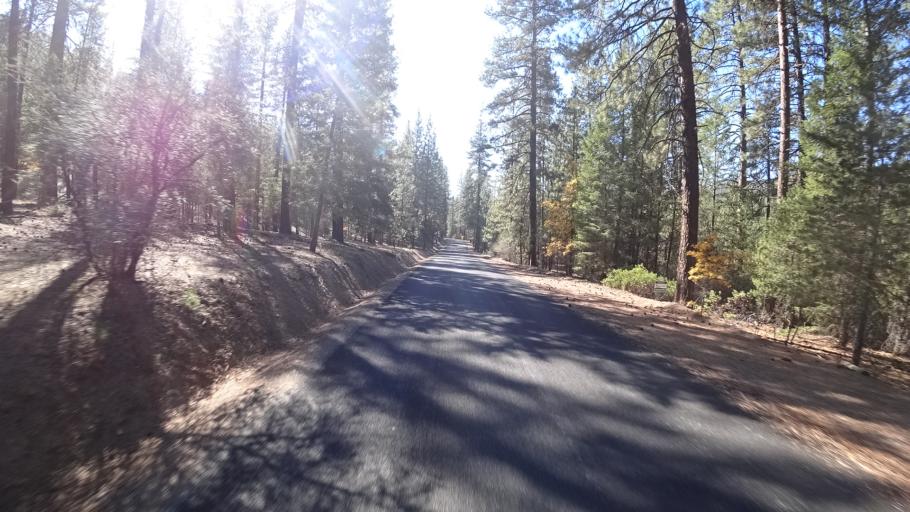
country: US
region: California
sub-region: Siskiyou County
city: Yreka
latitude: 41.6548
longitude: -122.8590
